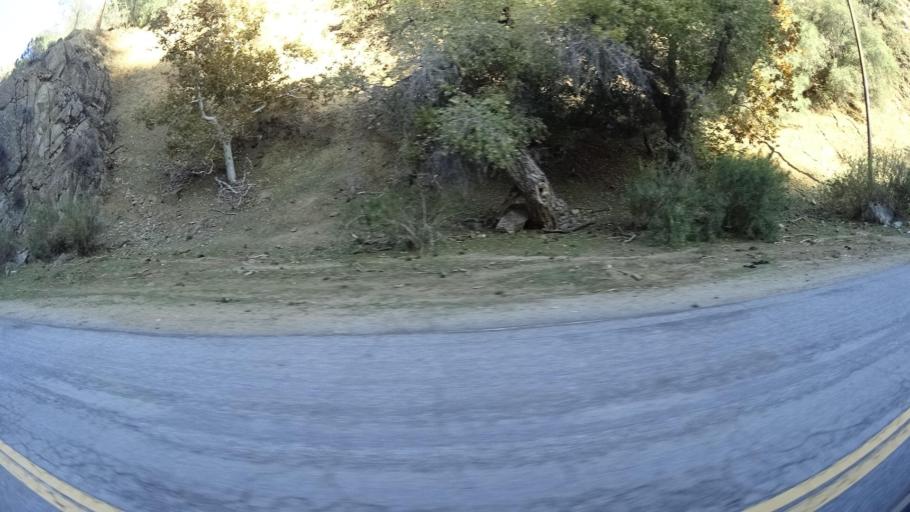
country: US
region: California
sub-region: Kern County
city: Golden Hills
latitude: 35.3151
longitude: -118.5164
